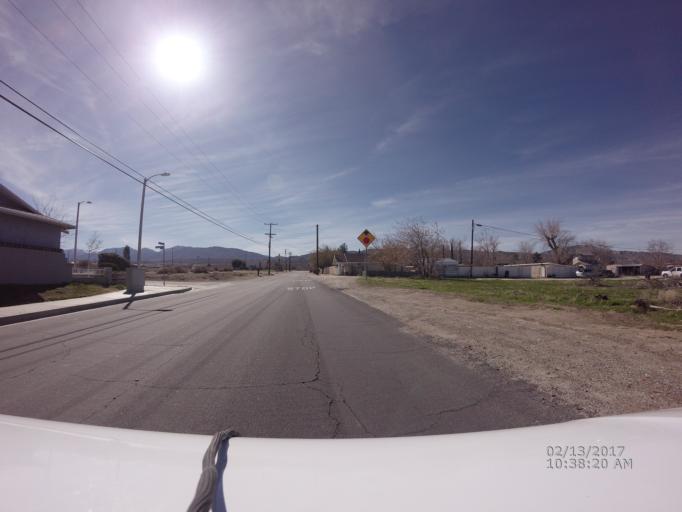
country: US
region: California
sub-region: Los Angeles County
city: Littlerock
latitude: 34.5232
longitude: -117.9793
